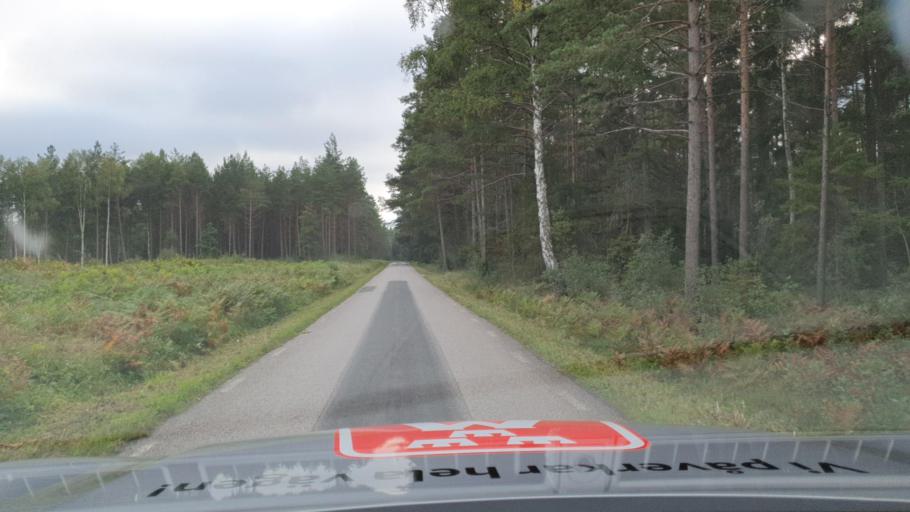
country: SE
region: Gotland
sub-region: Gotland
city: Vibble
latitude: 57.5047
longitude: 18.2634
